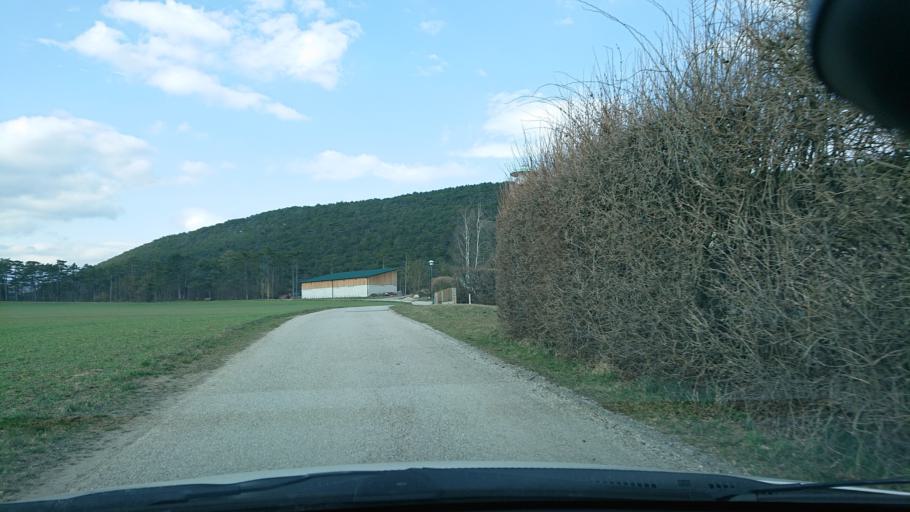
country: AT
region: Lower Austria
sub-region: Politischer Bezirk Baden
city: Berndorf
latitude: 47.9275
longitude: 16.1111
